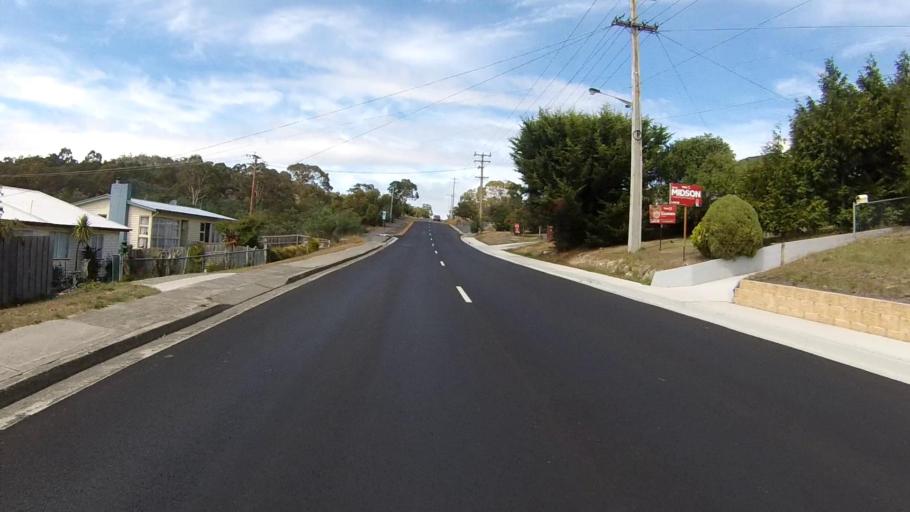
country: AU
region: Tasmania
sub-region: Clarence
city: Lindisfarne
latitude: -42.8143
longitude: 147.3513
